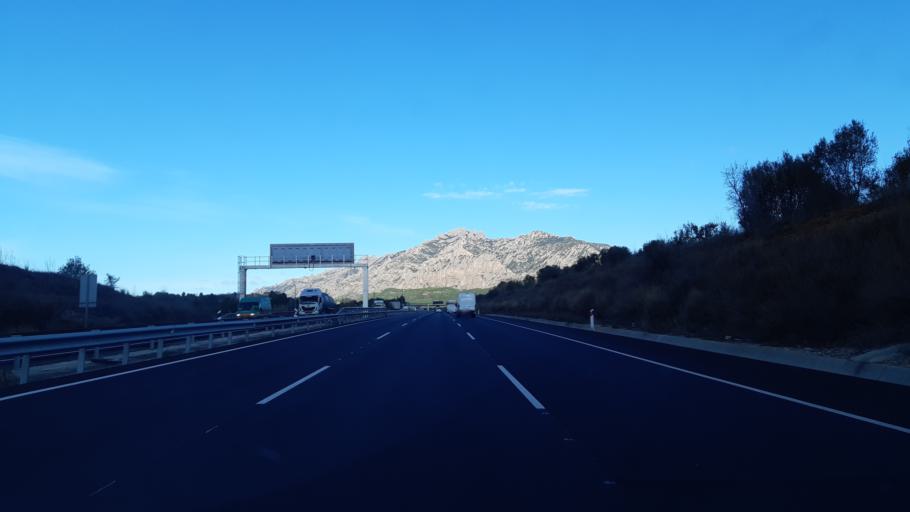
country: ES
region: Catalonia
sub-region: Provincia de Barcelona
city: Esparreguera
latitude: 41.5391
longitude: 1.8582
